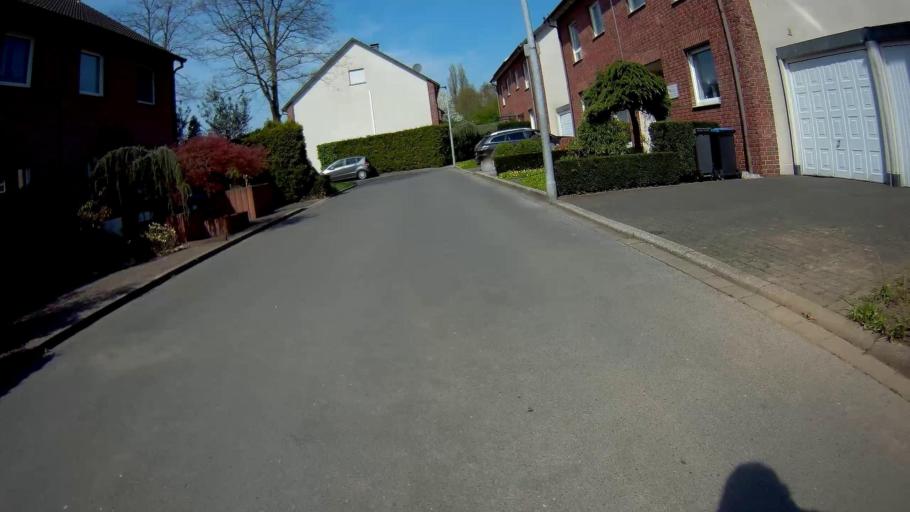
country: DE
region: North Rhine-Westphalia
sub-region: Regierungsbezirk Munster
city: Gladbeck
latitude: 51.5574
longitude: 7.0512
